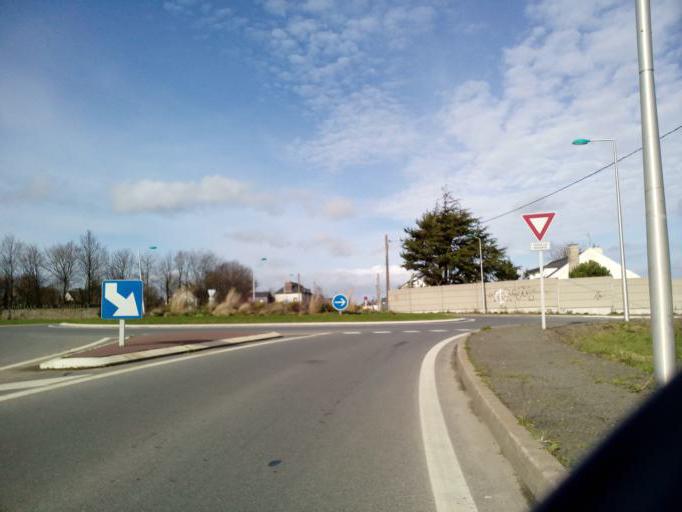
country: FR
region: Brittany
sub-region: Departement d'Ille-et-Vilaine
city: La Chapelle-des-Fougeretz
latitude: 48.1739
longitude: -1.7211
